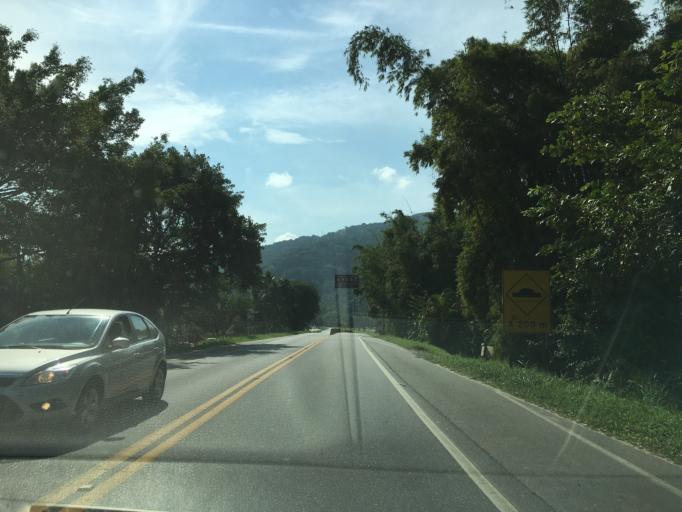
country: BR
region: Sao Paulo
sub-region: Sao Sebastiao
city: Sao Sebastiao
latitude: -23.7656
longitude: -45.7208
